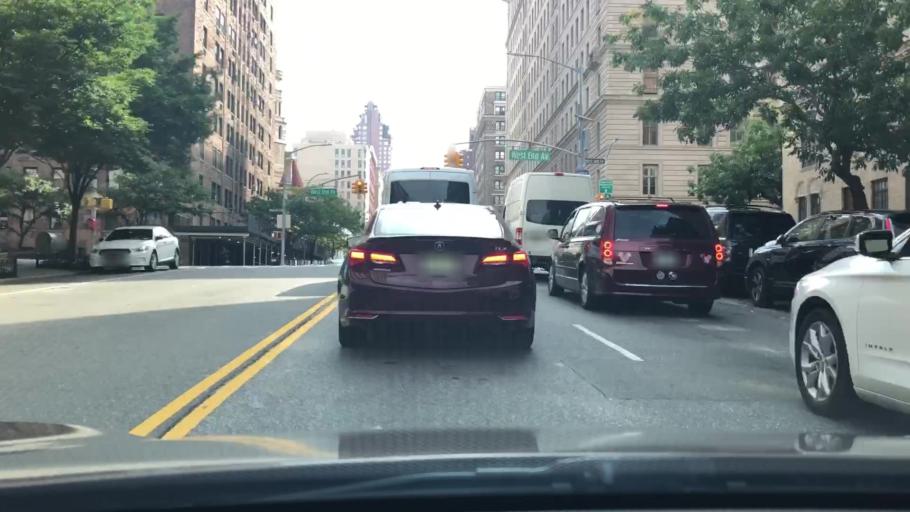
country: US
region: New York
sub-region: New York County
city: Manhattan
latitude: 40.7846
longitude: -73.9817
